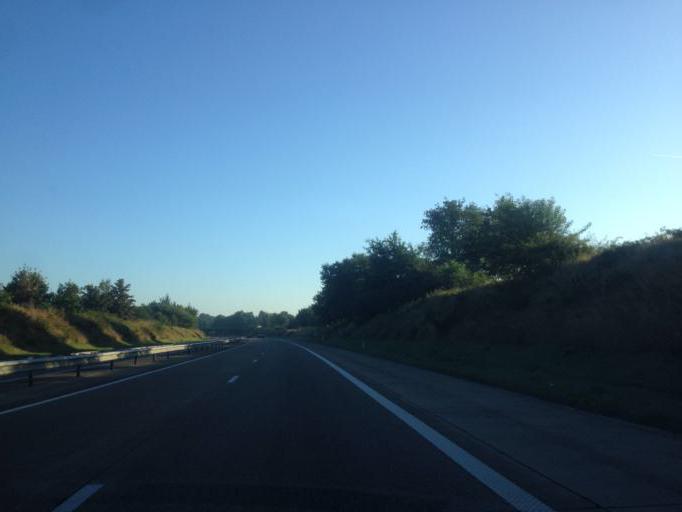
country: BE
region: Flanders
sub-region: Provincie Limburg
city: Peer
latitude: 51.1475
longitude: 5.4054
